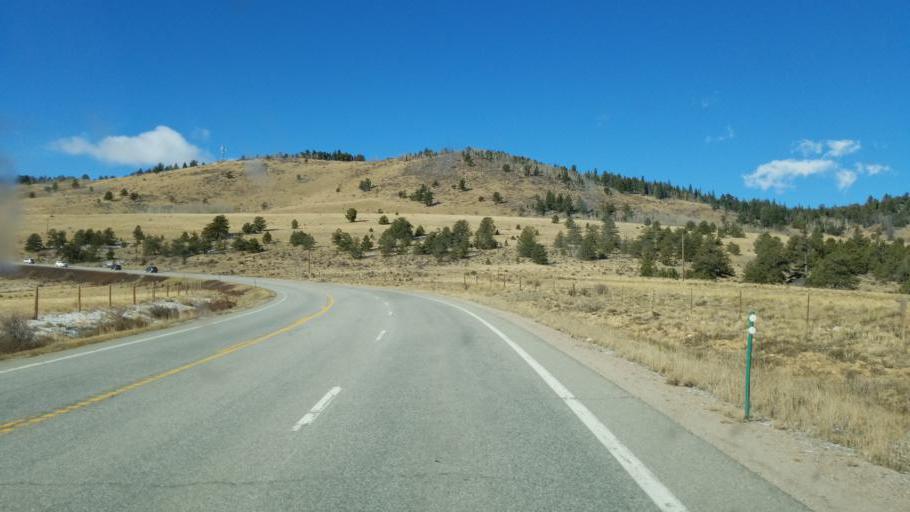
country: US
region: Colorado
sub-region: Park County
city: Fairplay
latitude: 39.2765
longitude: -105.9497
